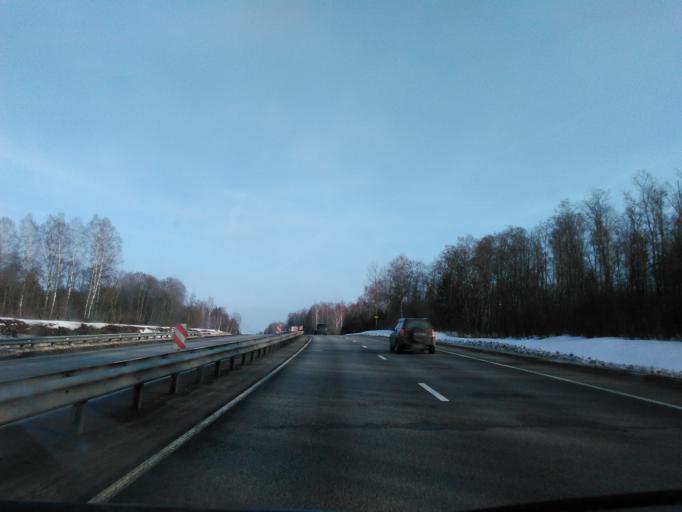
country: RU
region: Smolensk
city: Vyaz'ma
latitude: 55.1913
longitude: 33.9550
